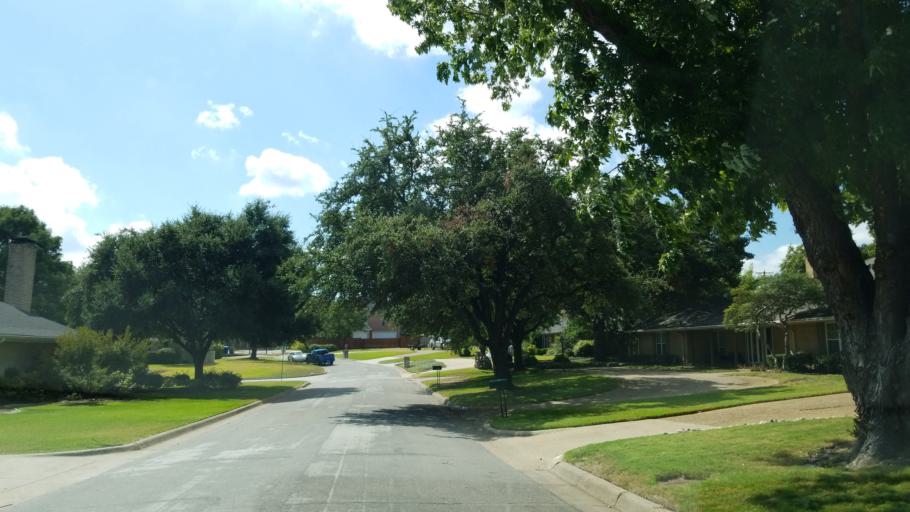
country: US
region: Texas
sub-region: Dallas County
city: Addison
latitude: 32.9318
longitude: -96.8017
